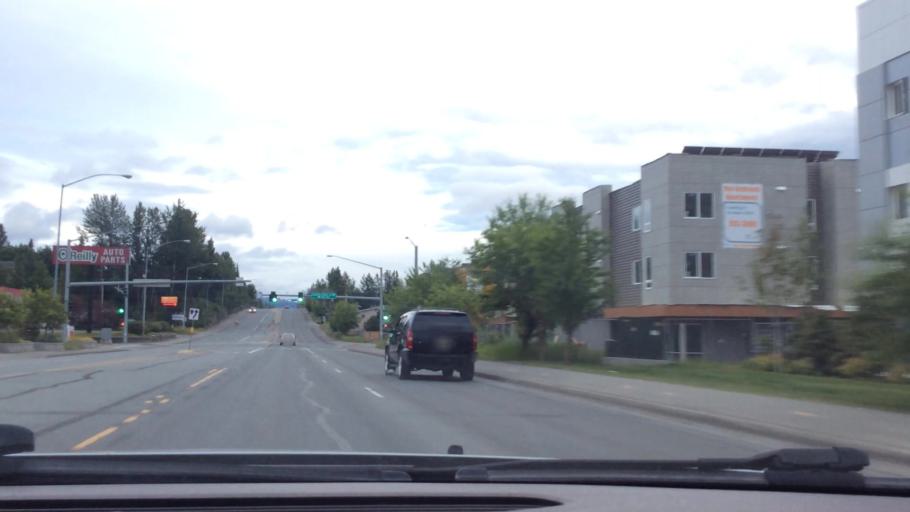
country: US
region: Alaska
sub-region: Anchorage Municipality
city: Elmendorf Air Force Base
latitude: 61.2080
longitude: -149.7335
